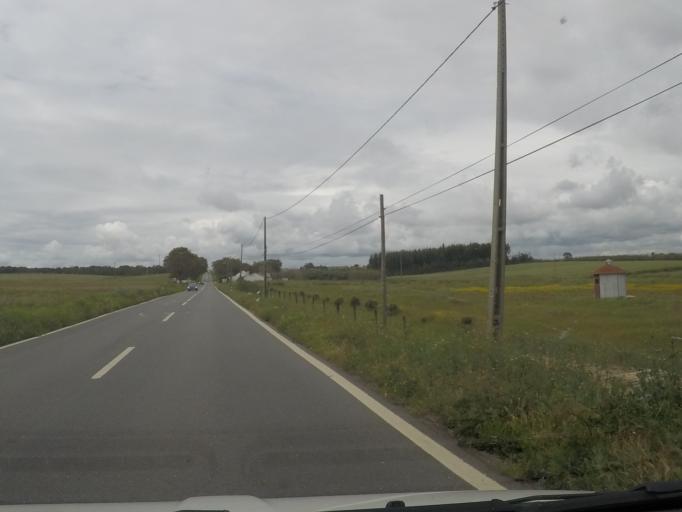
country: PT
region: Setubal
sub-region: Santiago do Cacem
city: Cercal
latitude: 37.8589
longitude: -8.7155
